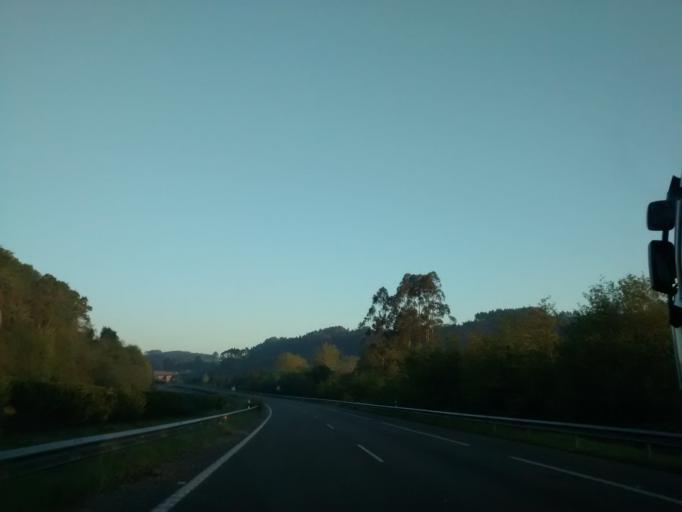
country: ES
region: Asturias
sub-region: Province of Asturias
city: Colunga
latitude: 43.4852
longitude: -5.3091
